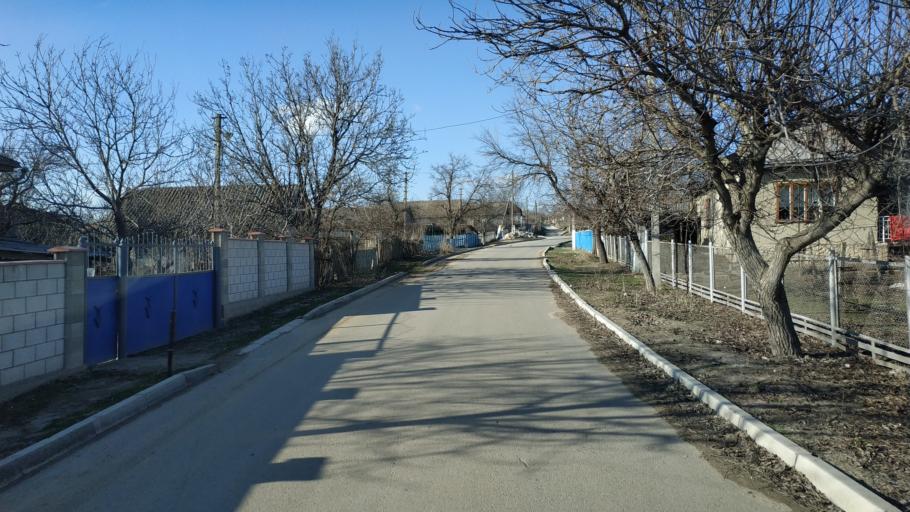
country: MD
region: Hincesti
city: Hincesti
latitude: 46.7297
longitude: 28.5135
